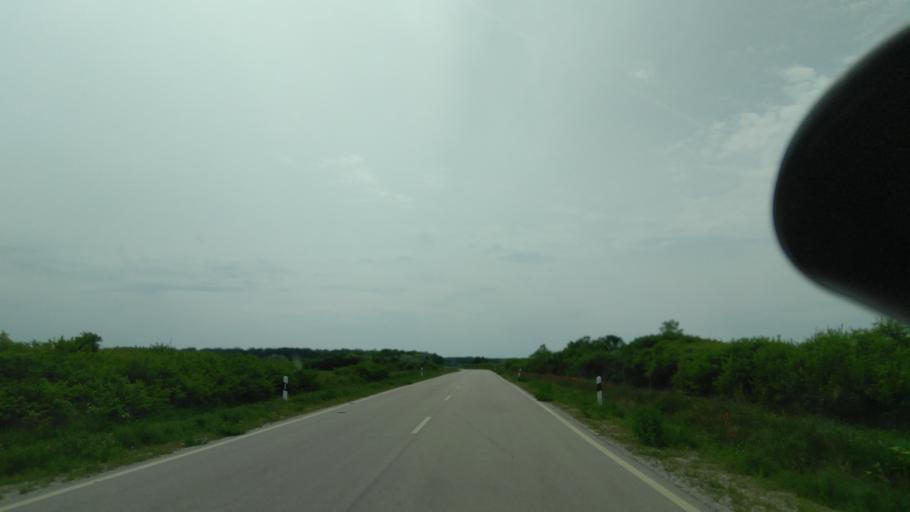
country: HU
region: Bekes
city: Mehkerek
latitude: 46.8636
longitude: 21.4631
